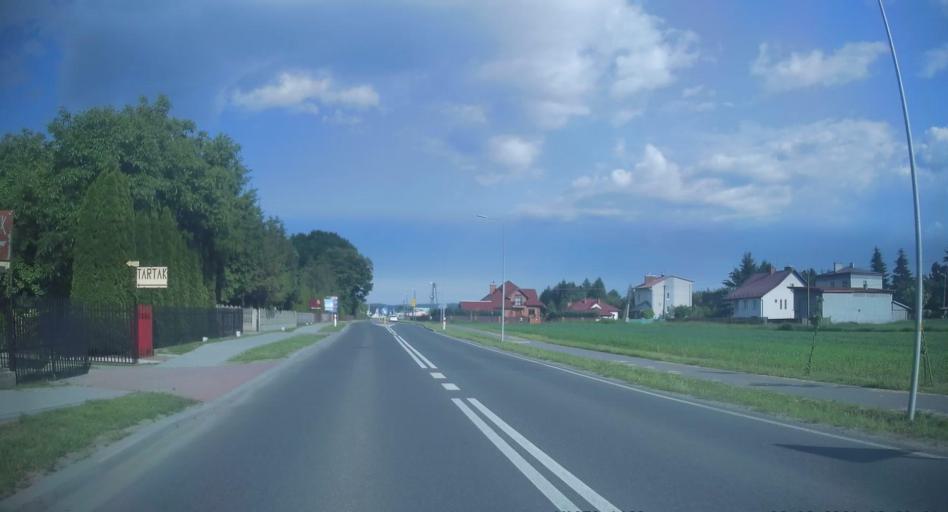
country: PL
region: Subcarpathian Voivodeship
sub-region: Powiat debicki
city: Zyrakow
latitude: 50.0729
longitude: 21.3918
